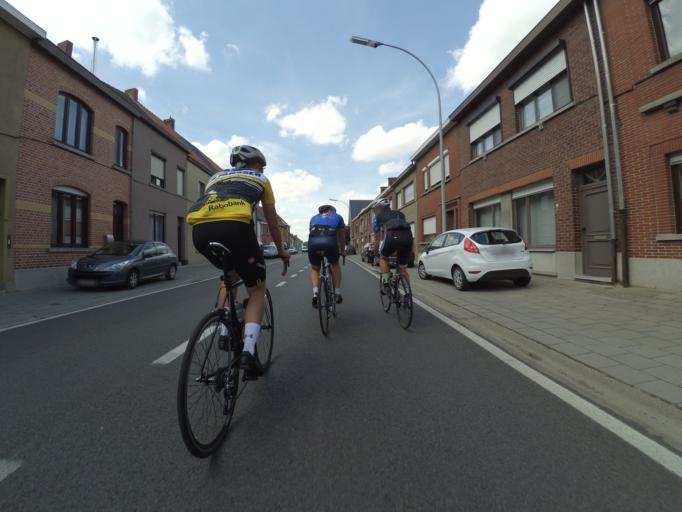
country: BE
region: Flanders
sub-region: Provincie Oost-Vlaanderen
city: Zottegem
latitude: 50.8675
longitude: 3.7989
